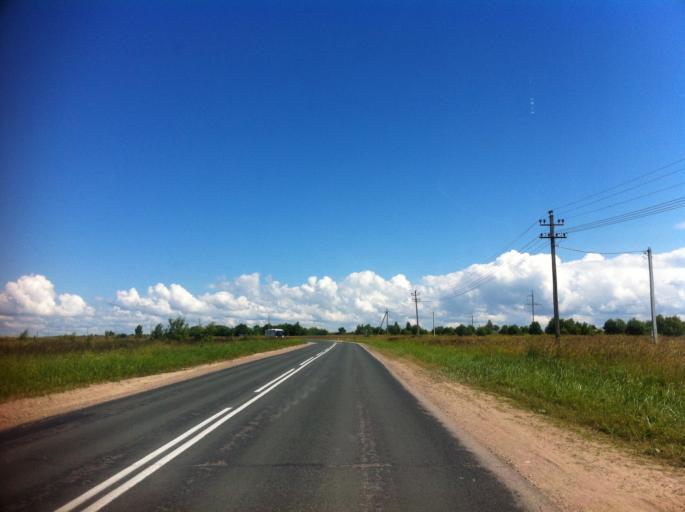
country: RU
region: Pskov
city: Izborsk
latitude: 57.8329
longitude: 27.9726
